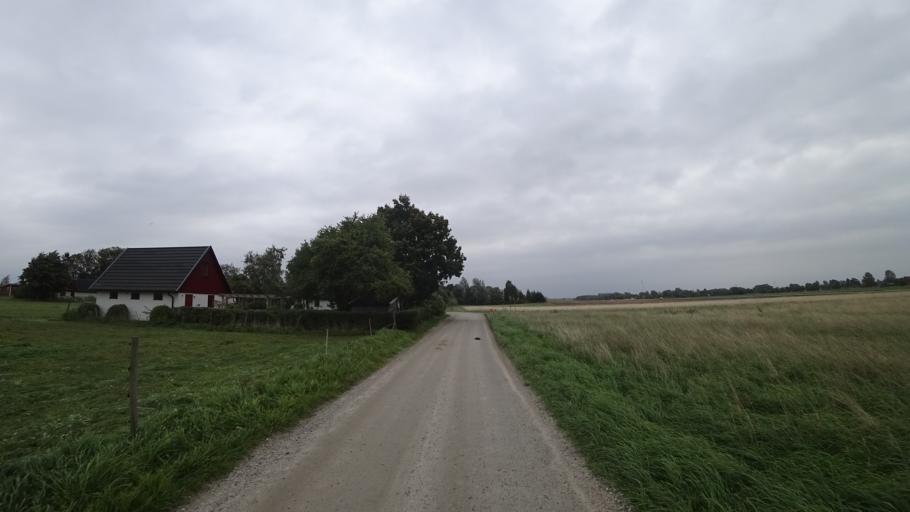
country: SE
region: Skane
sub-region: Kavlinge Kommun
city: Kaevlinge
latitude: 55.7991
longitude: 13.1396
